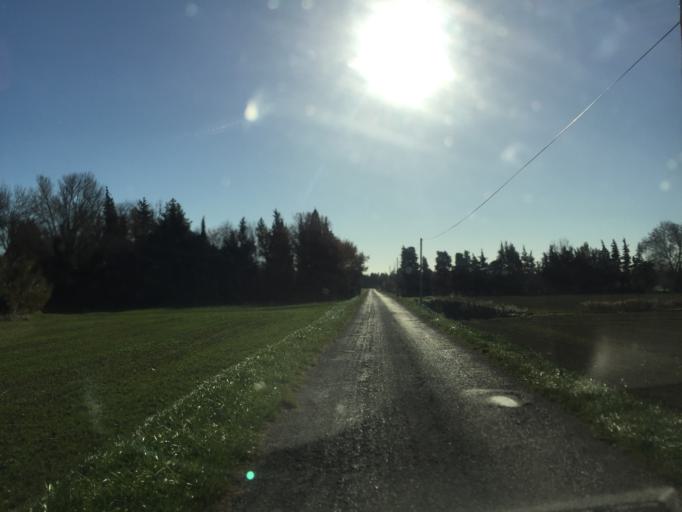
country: FR
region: Provence-Alpes-Cote d'Azur
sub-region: Departement du Vaucluse
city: Sarrians
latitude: 44.0748
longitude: 4.9274
